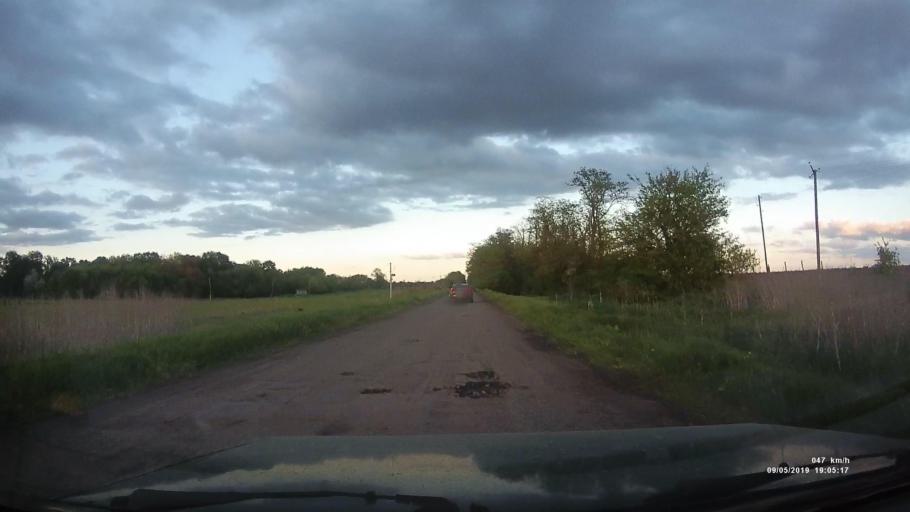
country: RU
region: Krasnodarskiy
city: Kanelovskaya
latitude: 46.7383
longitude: 39.1793
